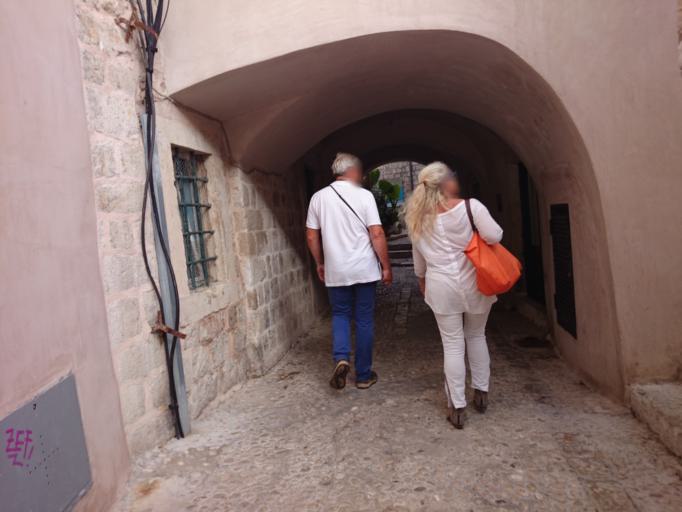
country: HR
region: Dubrovacko-Neretvanska
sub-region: Grad Dubrovnik
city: Dubrovnik
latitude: 42.6399
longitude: 18.1118
